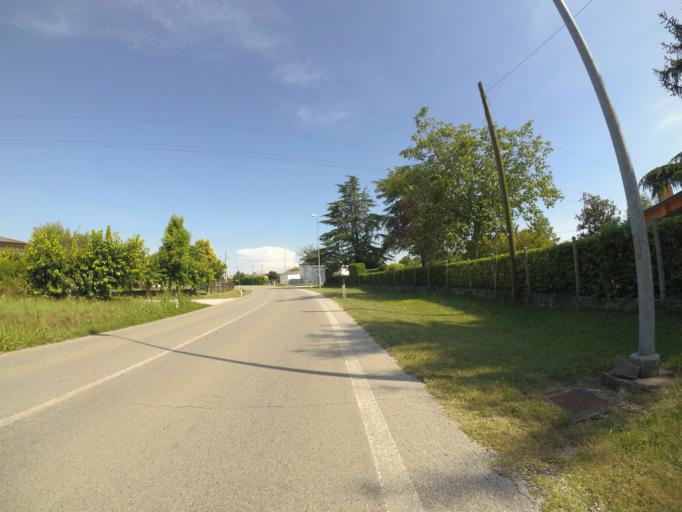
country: IT
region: Friuli Venezia Giulia
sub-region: Provincia di Udine
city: Mortegliano
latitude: 45.9506
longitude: 13.1631
